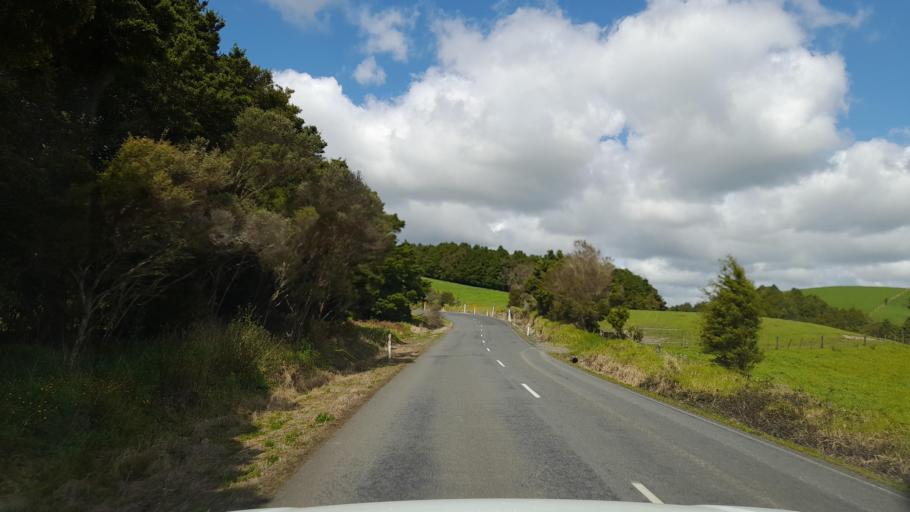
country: NZ
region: Northland
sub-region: Whangarei
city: Maungatapere
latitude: -35.6391
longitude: 174.0620
